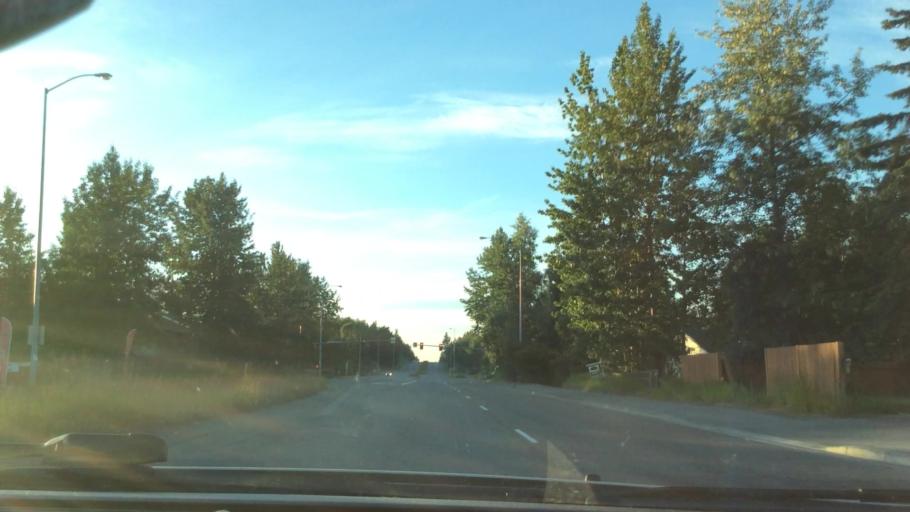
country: US
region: Alaska
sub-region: Anchorage Municipality
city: Anchorage
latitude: 61.1974
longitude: -149.7783
